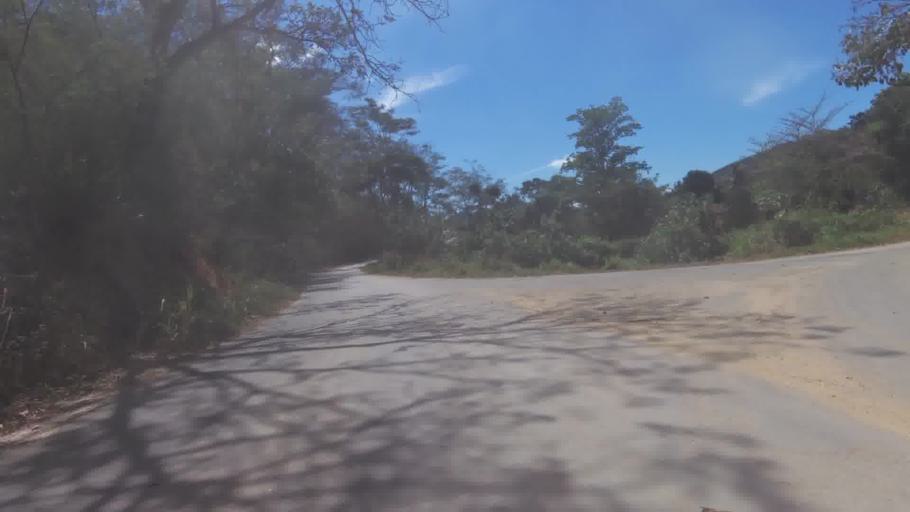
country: BR
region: Espirito Santo
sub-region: Cachoeiro De Itapemirim
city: Cachoeiro de Itapemirim
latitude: -20.9420
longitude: -41.2219
